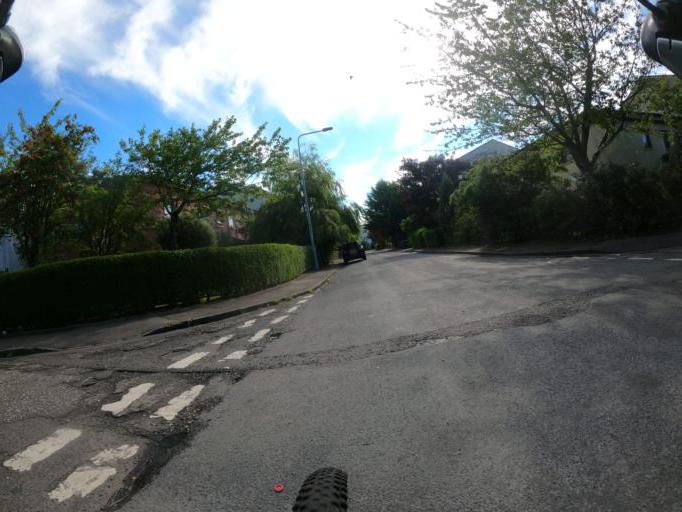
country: GB
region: Scotland
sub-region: Edinburgh
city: Edinburgh
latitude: 55.9695
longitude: -3.2441
